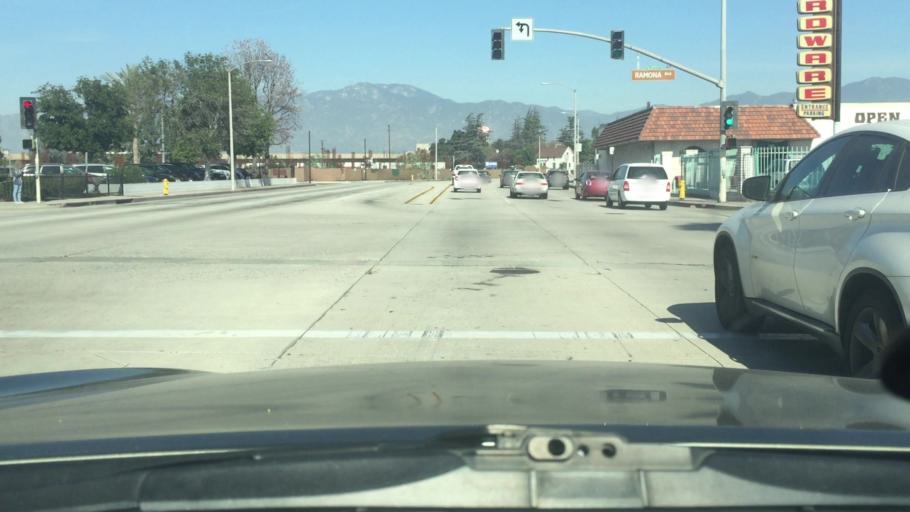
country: US
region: California
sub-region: Los Angeles County
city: El Monte
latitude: 34.0718
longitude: -118.0422
